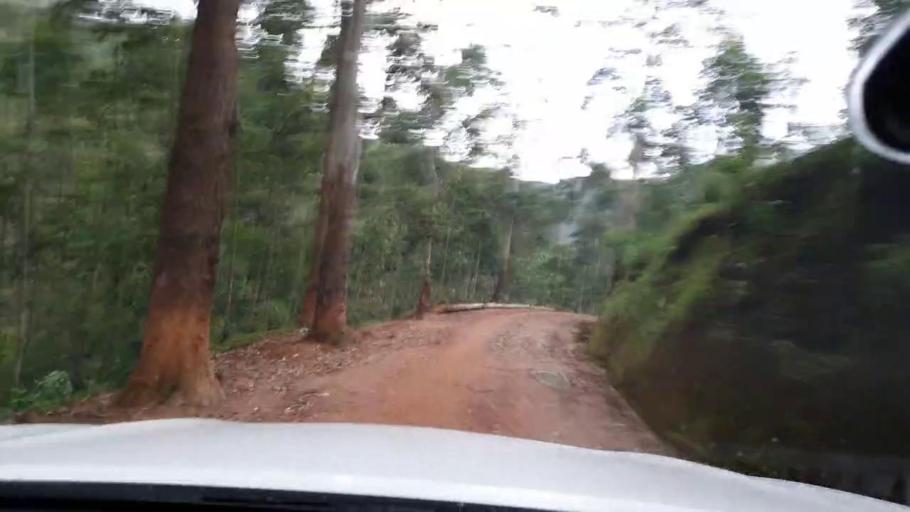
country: RW
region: Western Province
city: Cyangugu
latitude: -2.4078
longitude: 29.2072
